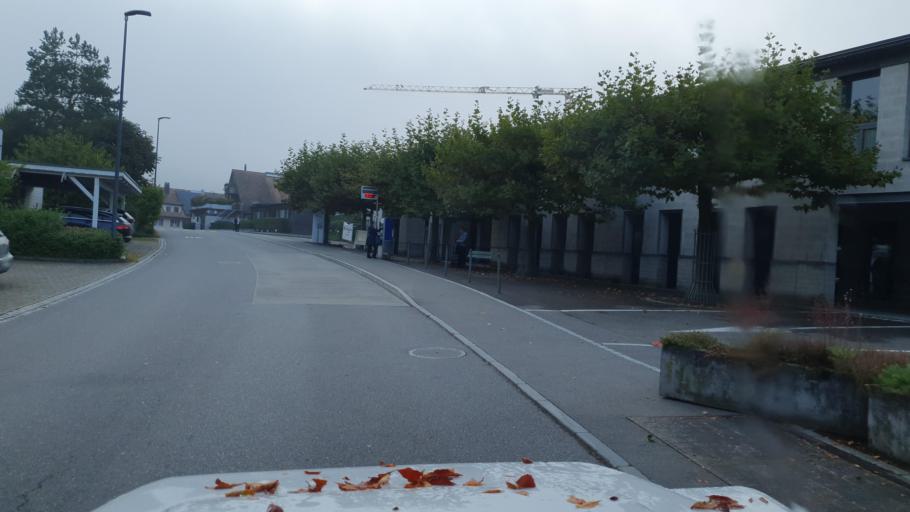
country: CH
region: Aargau
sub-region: Bezirk Baden
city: Baden
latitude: 47.4544
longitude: 8.2840
